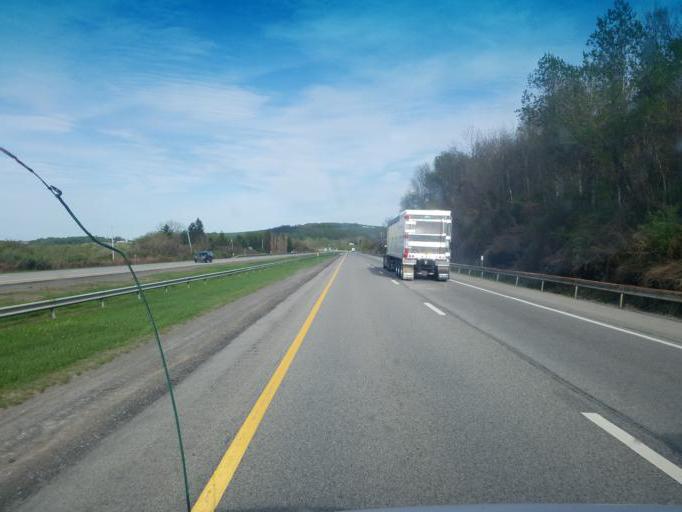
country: US
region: New York
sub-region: Herkimer County
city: Little Falls
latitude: 43.0063
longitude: -74.8979
